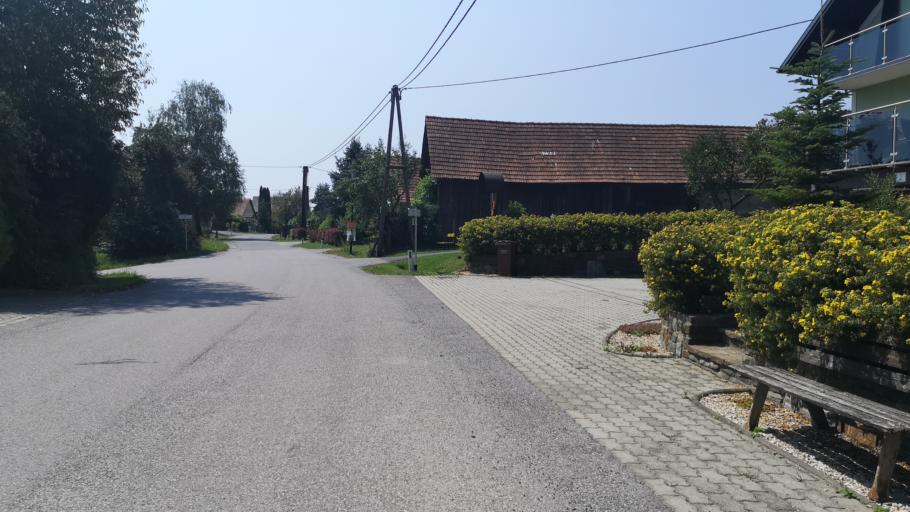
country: AT
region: Styria
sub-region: Politischer Bezirk Deutschlandsberg
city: Preding
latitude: 46.8684
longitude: 15.3898
